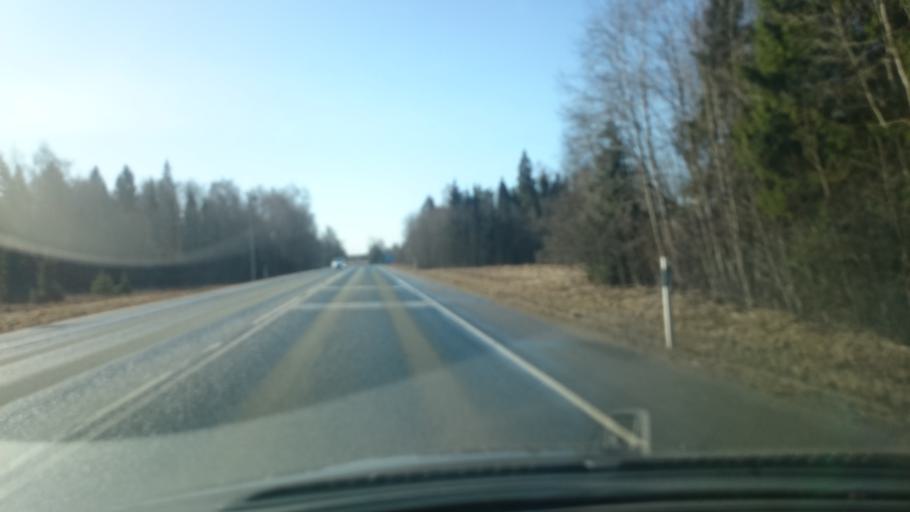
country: EE
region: Raplamaa
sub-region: Rapla vald
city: Rapla
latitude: 59.0458
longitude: 24.8385
